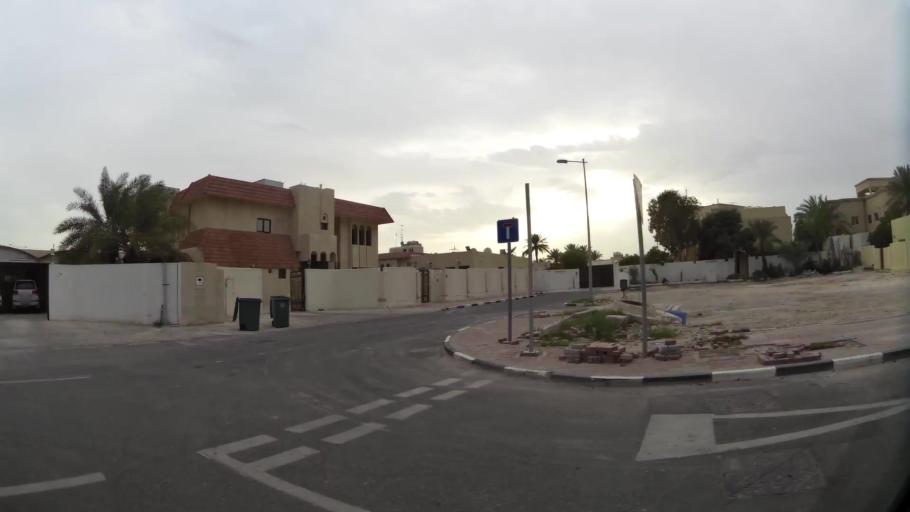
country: QA
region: Baladiyat ad Dawhah
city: Doha
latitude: 25.3263
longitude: 51.5089
